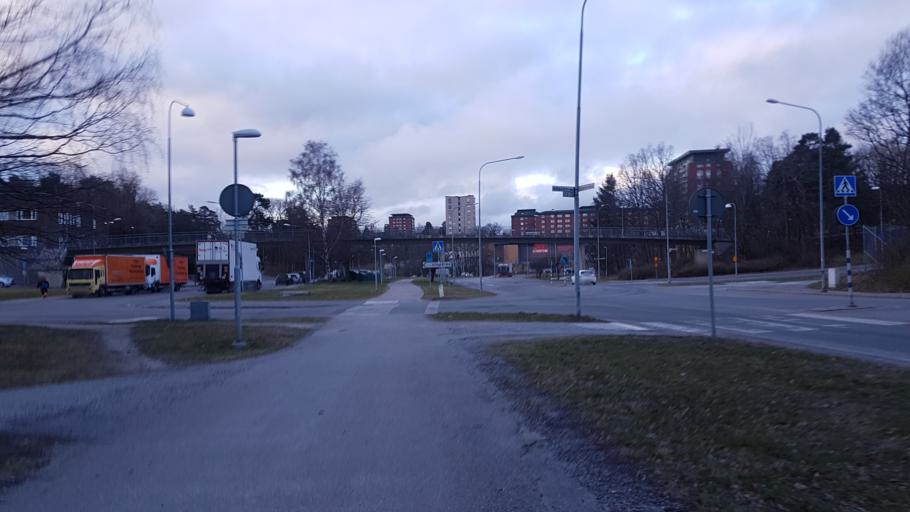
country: SE
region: Stockholm
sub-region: Lidingo
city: Lidingoe
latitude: 59.3520
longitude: 18.1490
